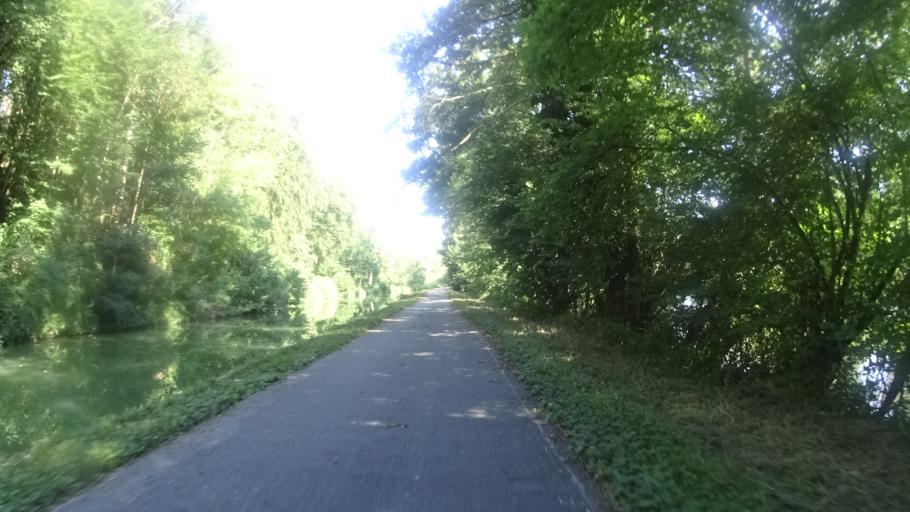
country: FR
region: Franche-Comte
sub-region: Departement du Doubs
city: Montenois
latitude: 47.4357
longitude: 6.5992
